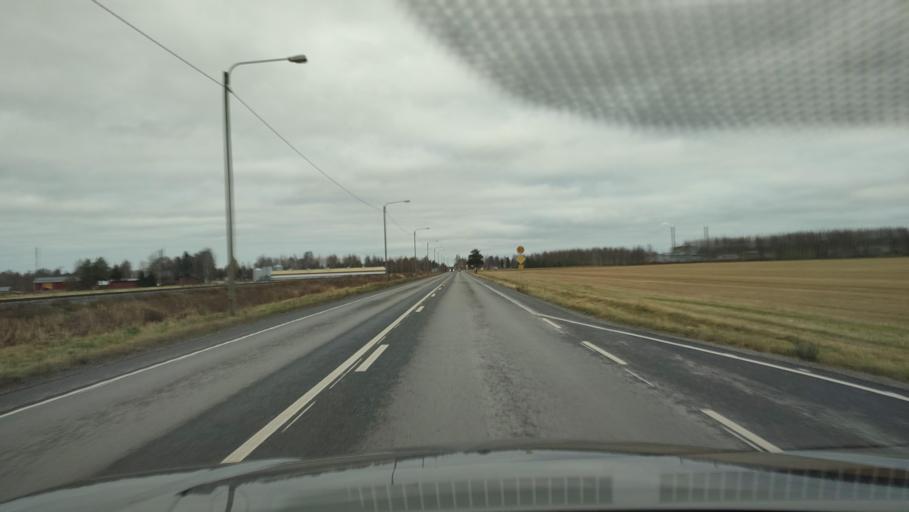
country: FI
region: Southern Ostrobothnia
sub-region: Seinaejoki
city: Ilmajoki
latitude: 62.7218
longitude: 22.5685
